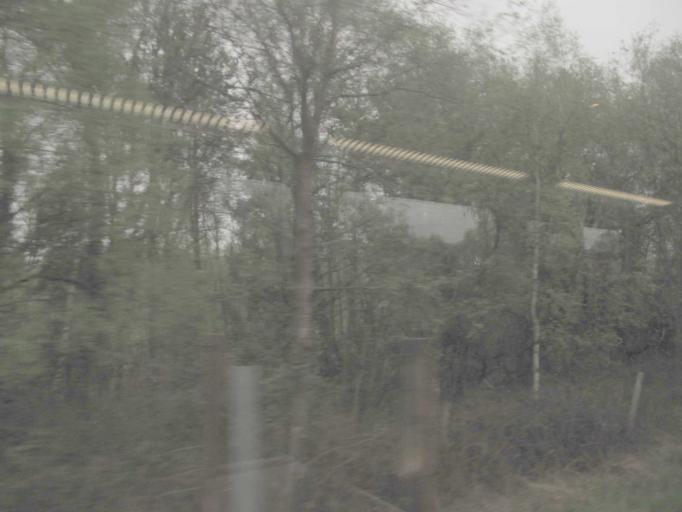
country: GB
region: England
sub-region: Surrey
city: Frimley
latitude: 51.3054
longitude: -0.7446
